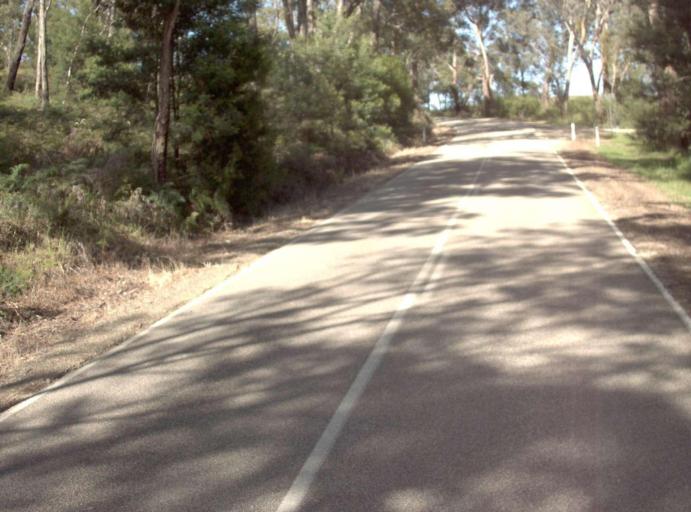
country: AU
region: Victoria
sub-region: East Gippsland
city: Lakes Entrance
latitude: -37.7432
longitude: 147.8158
